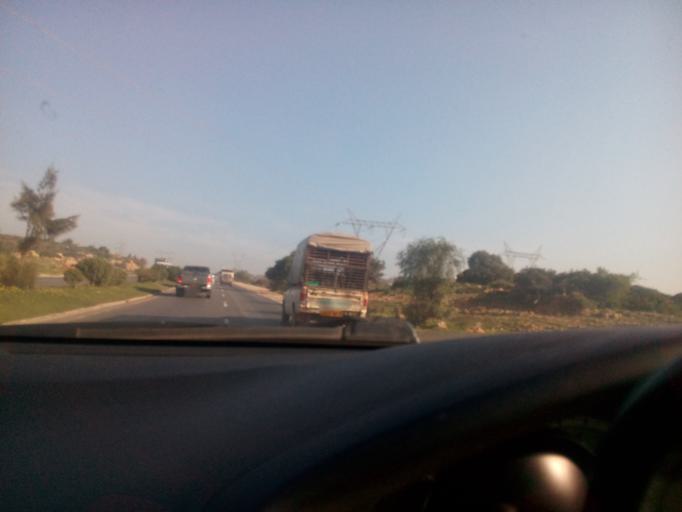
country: DZ
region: Oran
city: Oran
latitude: 35.6413
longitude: -0.7097
